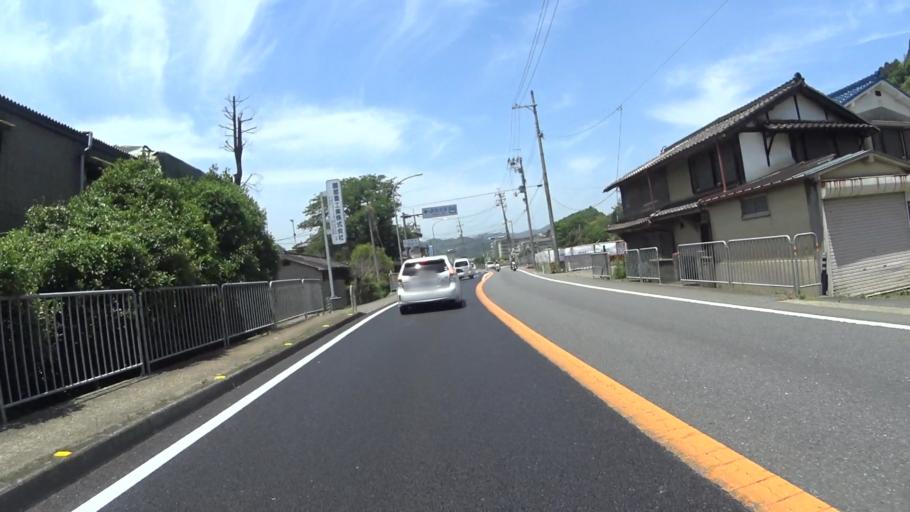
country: JP
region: Kyoto
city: Kameoka
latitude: 35.1028
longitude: 135.4860
